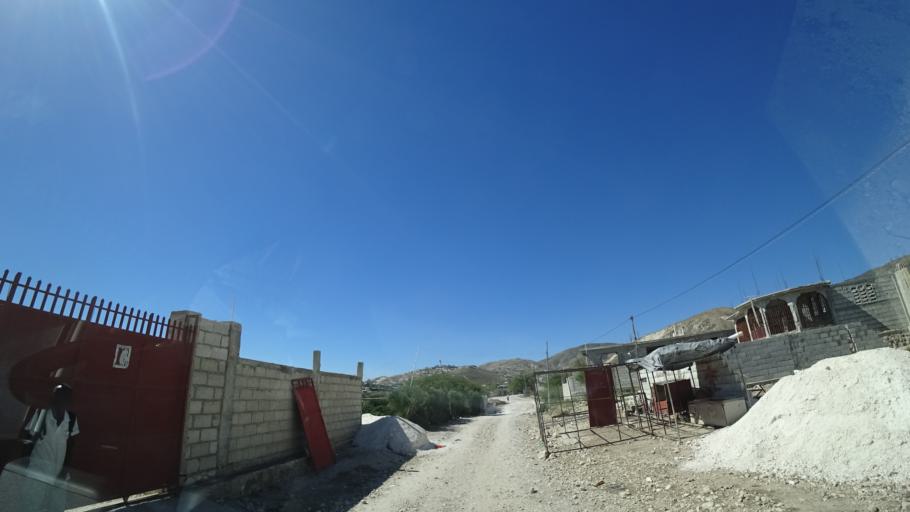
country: HT
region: Ouest
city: Croix des Bouquets
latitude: 18.6711
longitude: -72.2392
